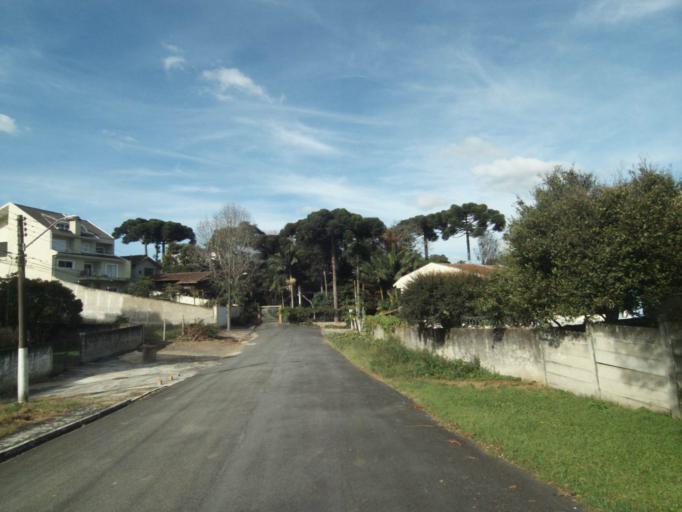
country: BR
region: Parana
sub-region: Curitiba
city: Curitiba
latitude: -25.4187
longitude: -49.2960
